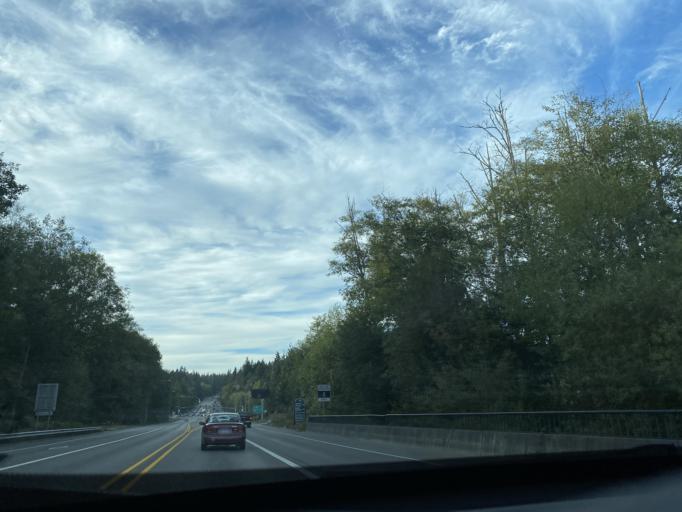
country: US
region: Washington
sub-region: Kitsap County
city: Poulsbo
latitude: 47.7494
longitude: -122.6425
